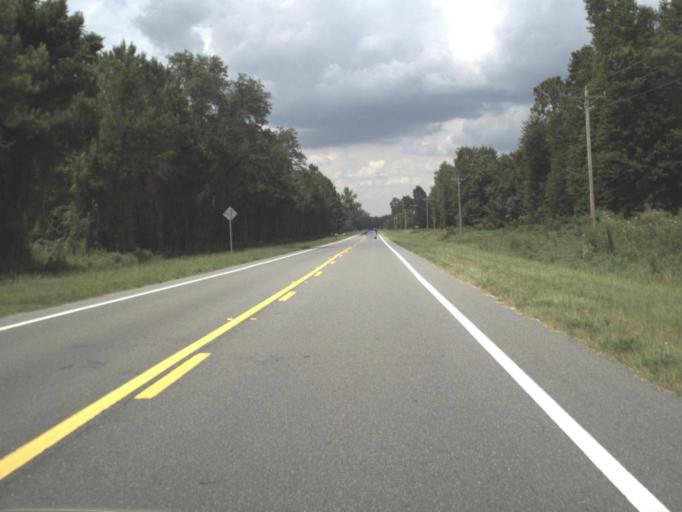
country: US
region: Florida
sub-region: Alachua County
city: Alachua
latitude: 29.8568
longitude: -82.3466
